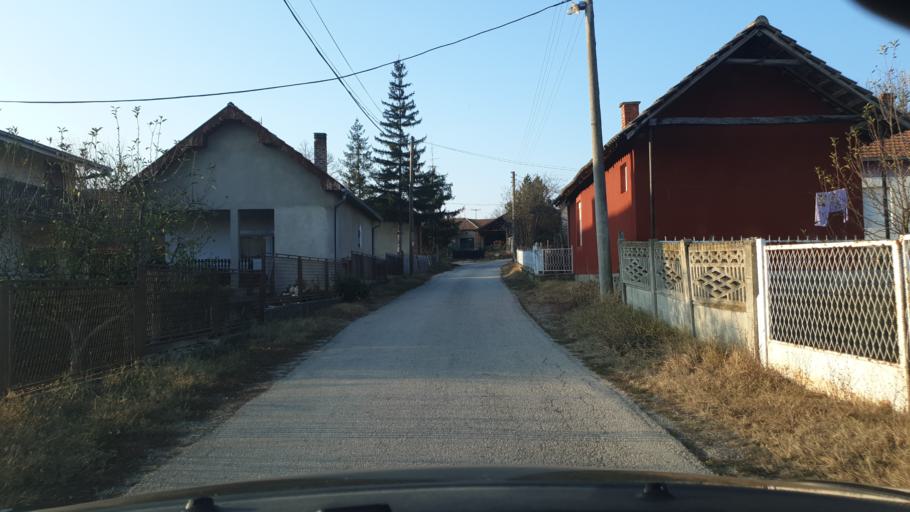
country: RS
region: Central Serbia
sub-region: Zajecarski Okrug
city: Zajecar
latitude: 44.0319
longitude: 22.3275
